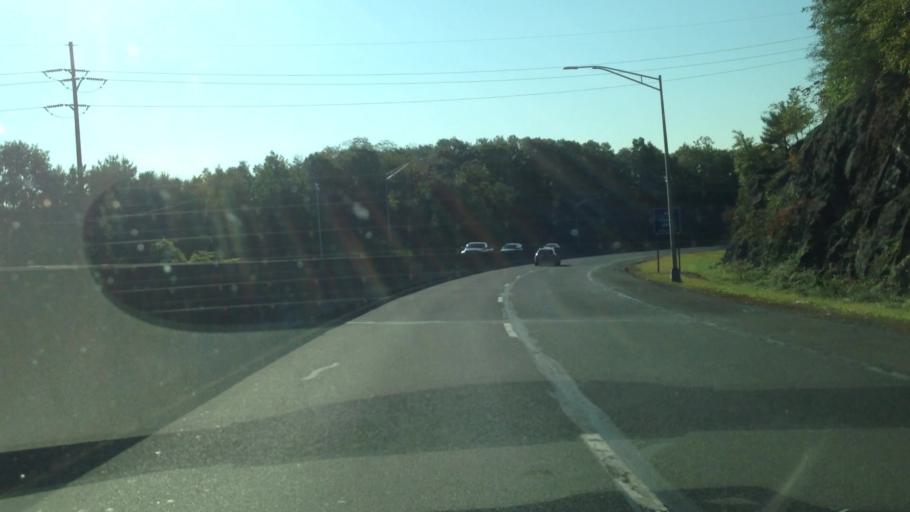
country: US
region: New York
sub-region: Ulster County
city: Highland
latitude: 41.7081
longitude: -73.9530
